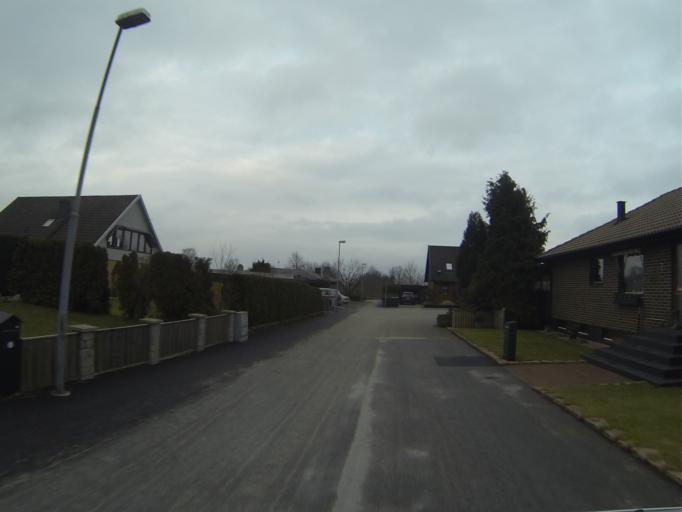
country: SE
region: Skane
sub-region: Lunds Kommun
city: Genarp
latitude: 55.7111
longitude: 13.3342
